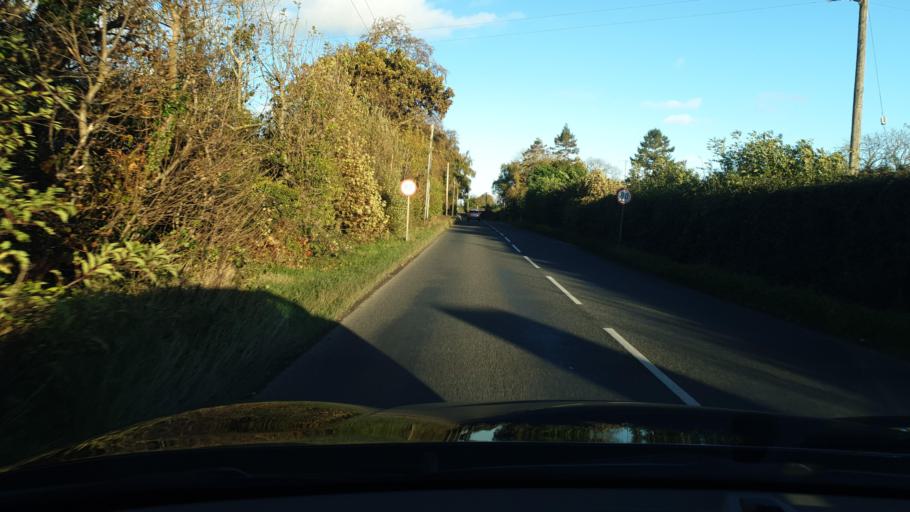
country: IE
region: Leinster
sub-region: Lu
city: Drogheda
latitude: 53.6925
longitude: -6.3420
